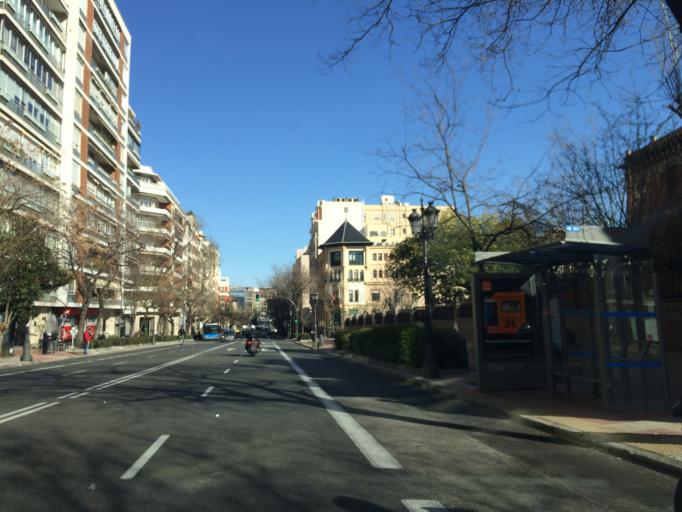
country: ES
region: Madrid
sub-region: Provincia de Madrid
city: Chamberi
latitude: 40.4328
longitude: -3.6944
